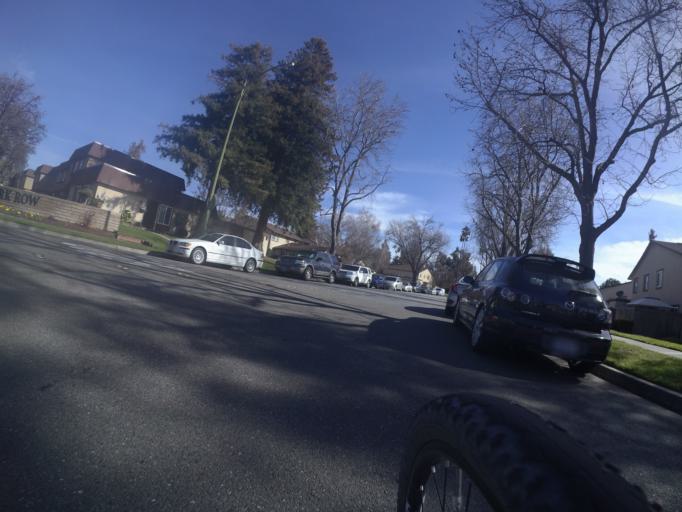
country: US
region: California
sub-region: Santa Clara County
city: Milpitas
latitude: 37.4118
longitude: -121.8624
